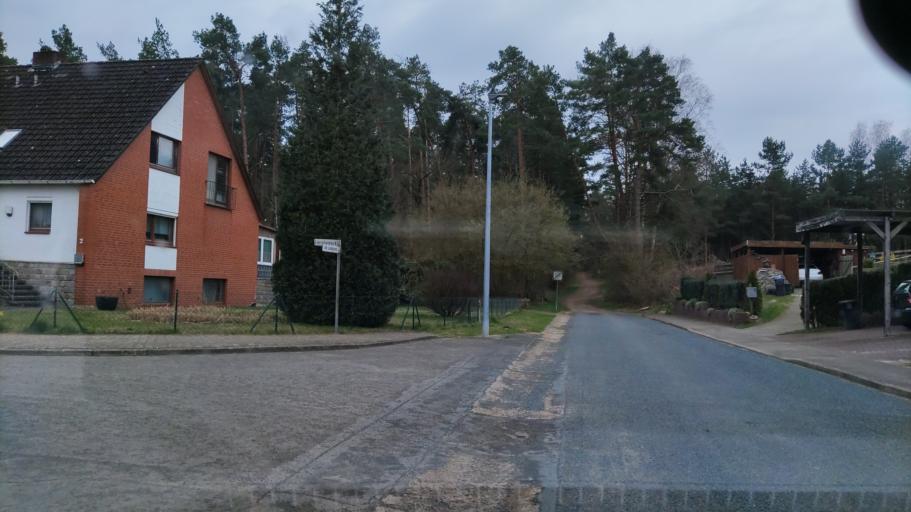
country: DE
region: Lower Saxony
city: Tosterglope
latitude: 53.2604
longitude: 10.7916
